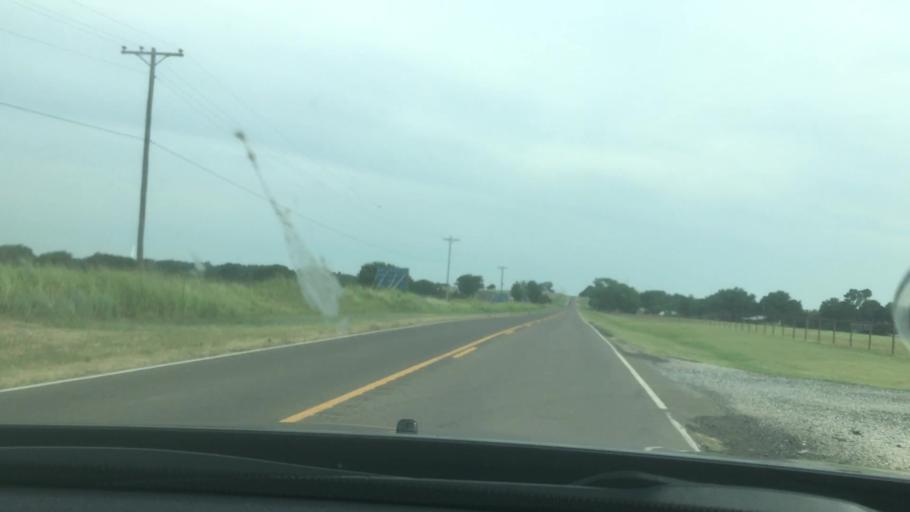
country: US
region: Oklahoma
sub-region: Garvin County
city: Pauls Valley
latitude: 34.7500
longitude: -97.2866
